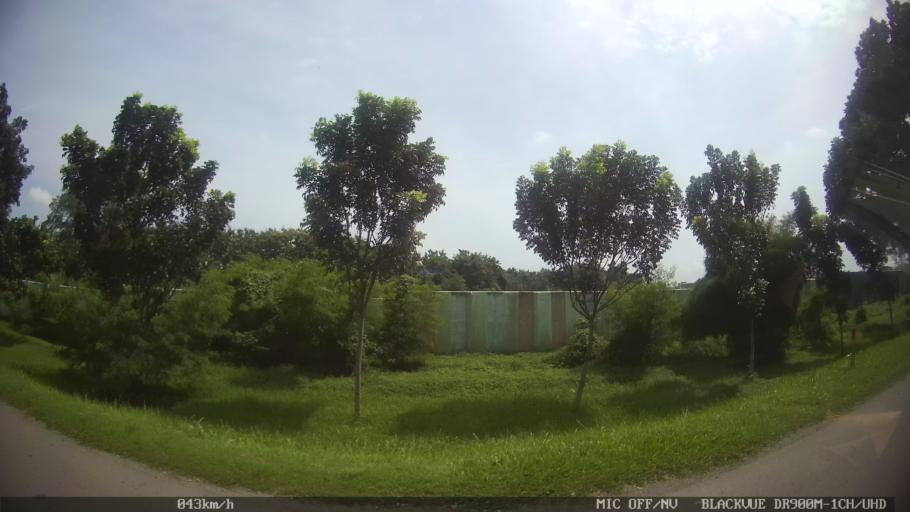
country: ID
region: North Sumatra
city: Medan
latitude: 3.6395
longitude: 98.7012
